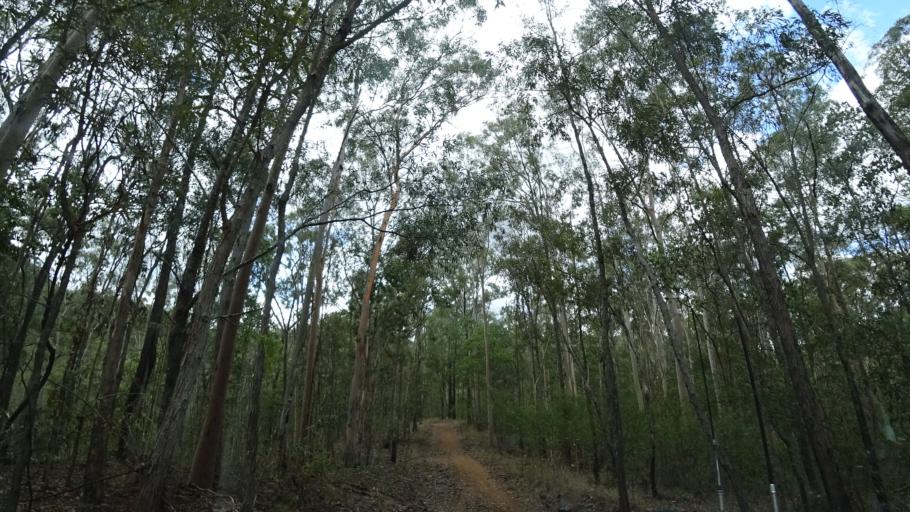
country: AU
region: Queensland
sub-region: Moreton Bay
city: Highvale
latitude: -27.4140
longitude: 152.7354
